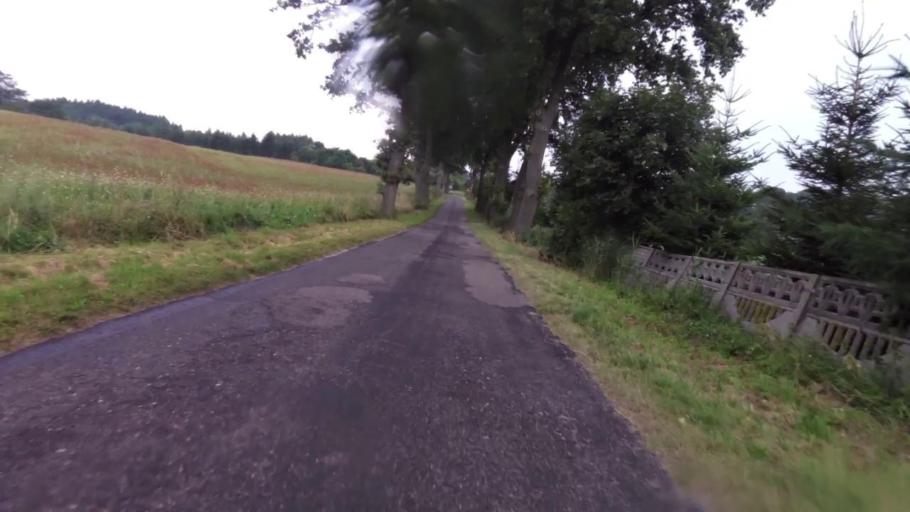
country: PL
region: West Pomeranian Voivodeship
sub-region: Powiat lobeski
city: Wegorzyno
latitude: 53.5132
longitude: 15.6485
